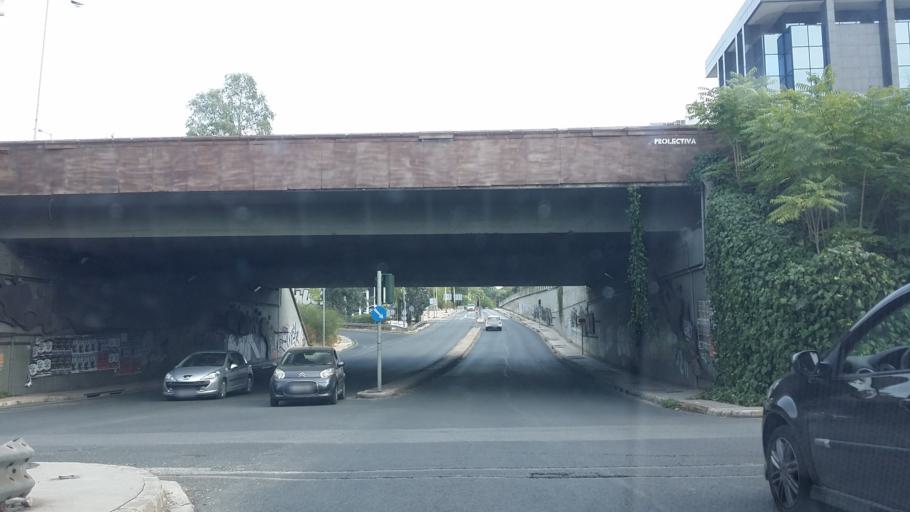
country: GR
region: Attica
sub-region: Nomarchia Athinas
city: Khalandrion
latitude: 38.0325
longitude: 23.7939
